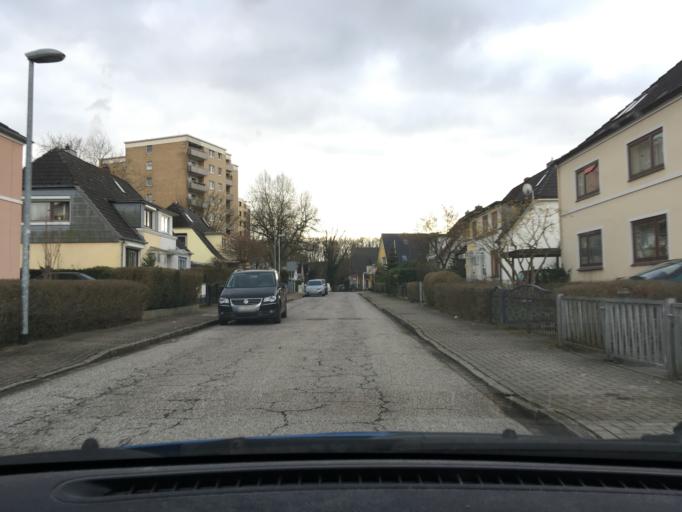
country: DE
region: Schleswig-Holstein
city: Wedel
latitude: 53.5774
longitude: 9.7175
